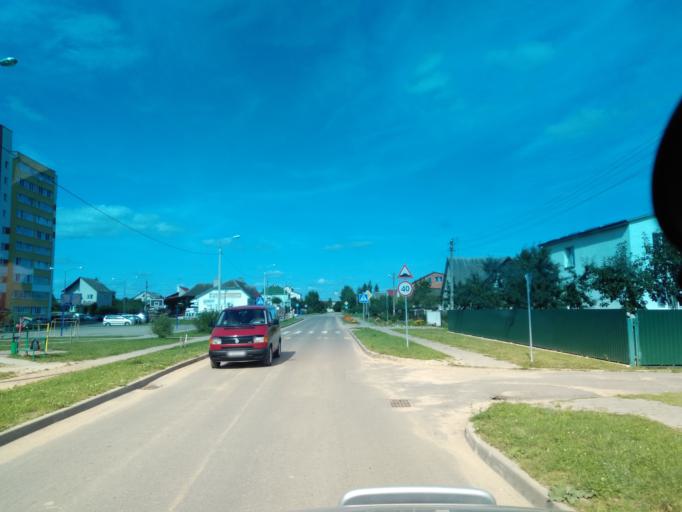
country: BY
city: Fanipol
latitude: 53.7518
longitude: 27.3358
